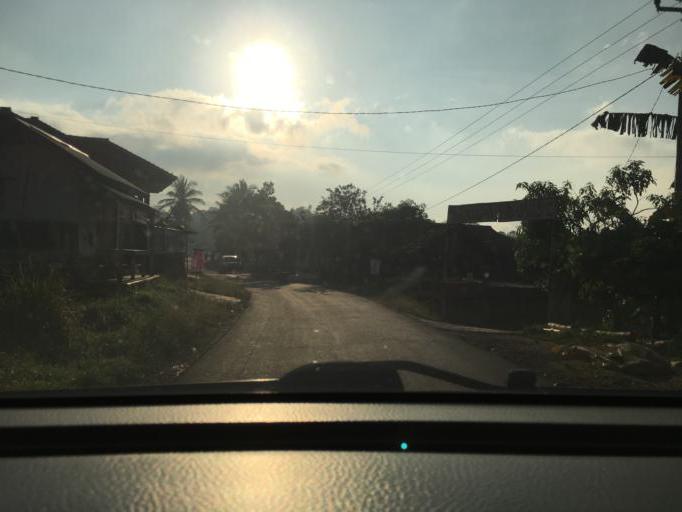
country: ID
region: West Java
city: Maniis
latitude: -7.0378
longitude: 108.3186
